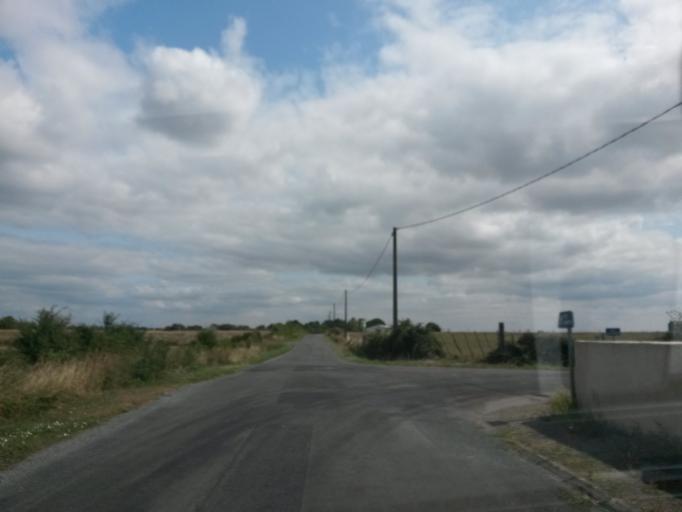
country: FR
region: Pays de la Loire
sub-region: Departement de la Vendee
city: Saint-Hilaire-de-Talmont
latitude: 46.4488
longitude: -1.6220
